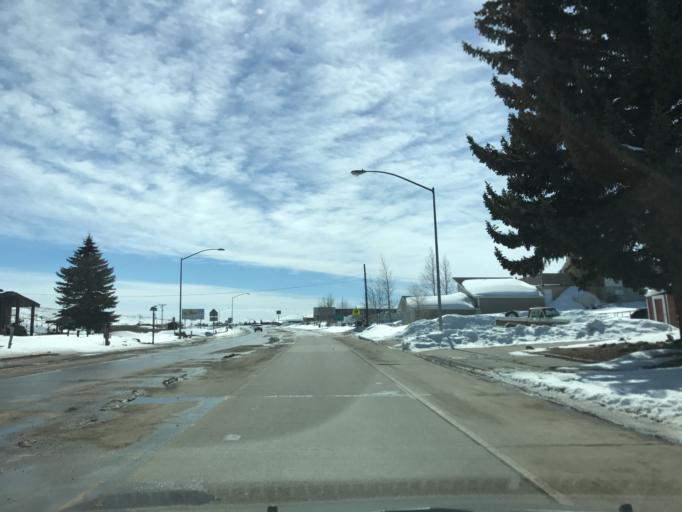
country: US
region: Wyoming
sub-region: Lincoln County
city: Kemmerer
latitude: 41.7875
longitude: -110.5392
